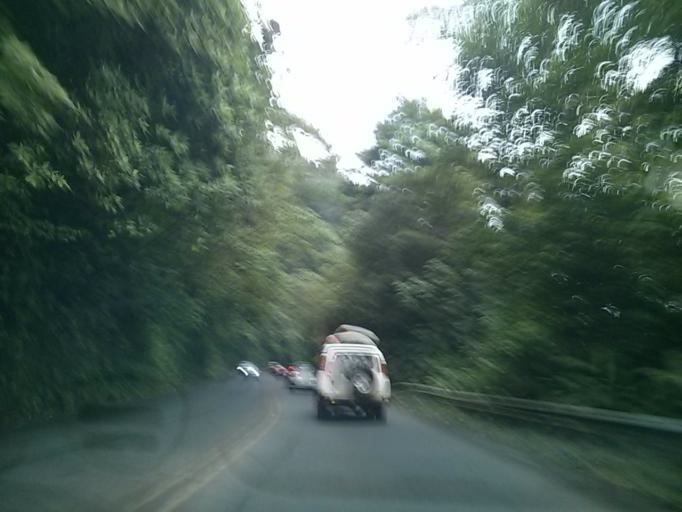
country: CR
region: San Jose
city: Dulce Nombre de Jesus
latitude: 10.1377
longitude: -83.9725
